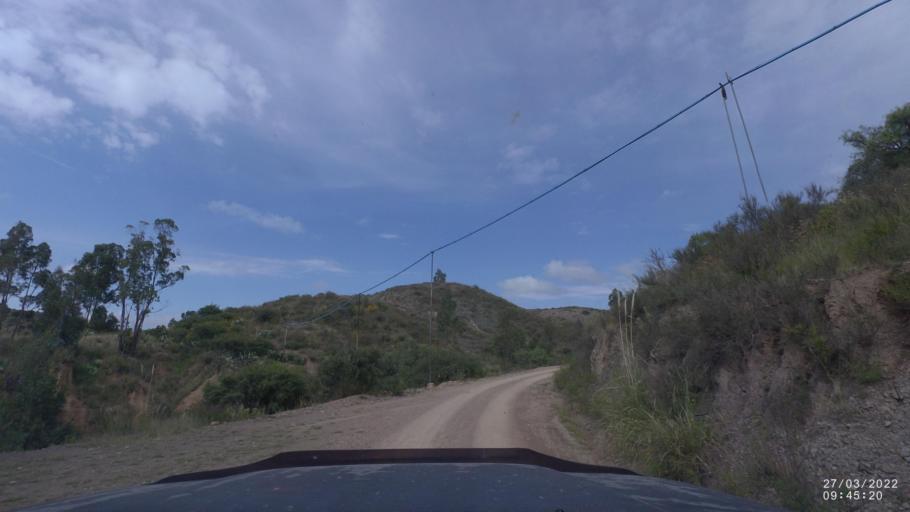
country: BO
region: Cochabamba
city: Cliza
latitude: -17.7507
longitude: -65.9130
